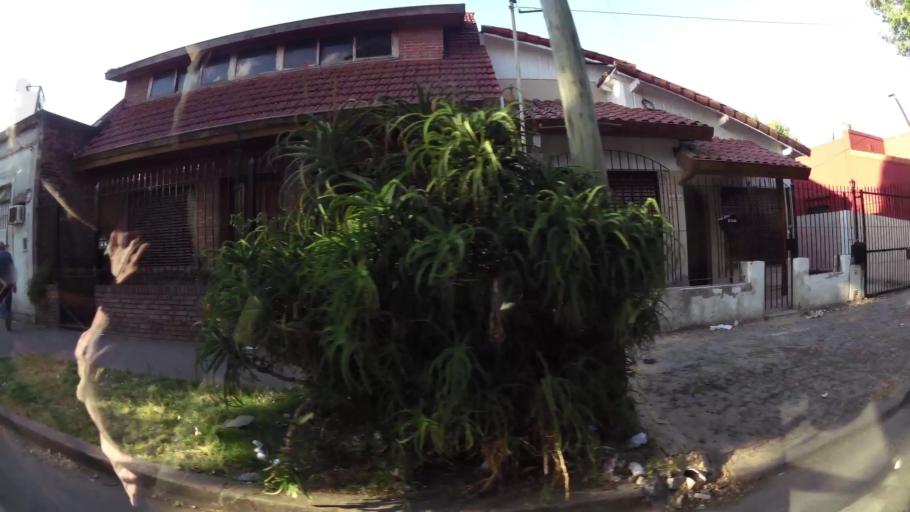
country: AR
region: Buenos Aires
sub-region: Partido de General San Martin
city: General San Martin
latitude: -34.5501
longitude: -58.5479
